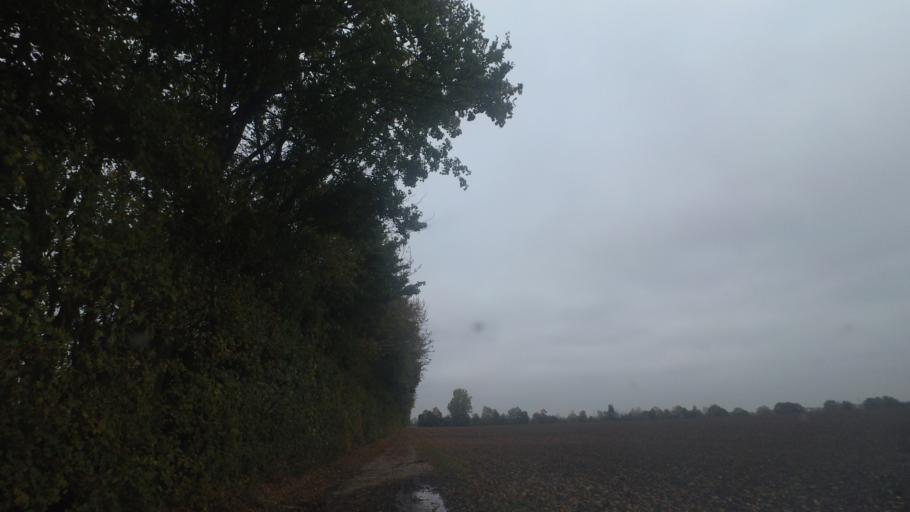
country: DE
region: Rheinland-Pfalz
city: Undenheim
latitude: 49.8258
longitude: 8.2115
